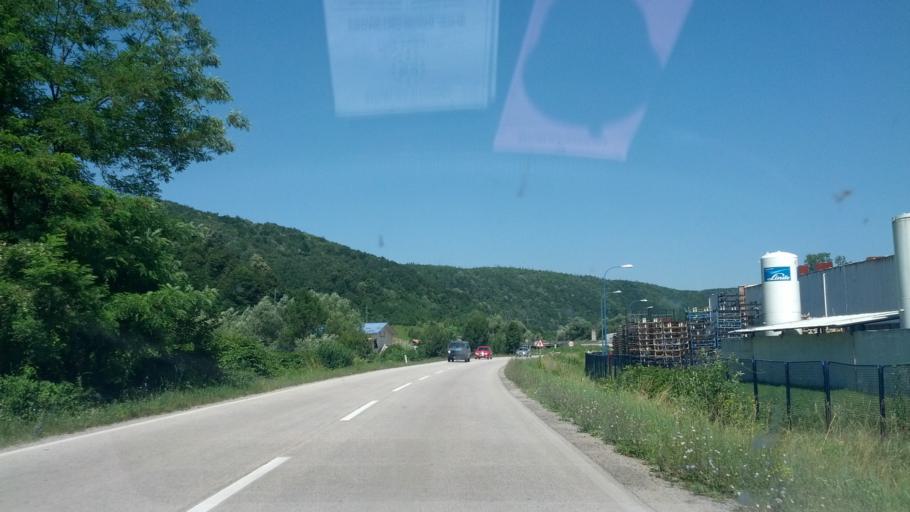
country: BA
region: Federation of Bosnia and Herzegovina
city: Bosanska Krupa
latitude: 44.9078
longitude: 16.1602
